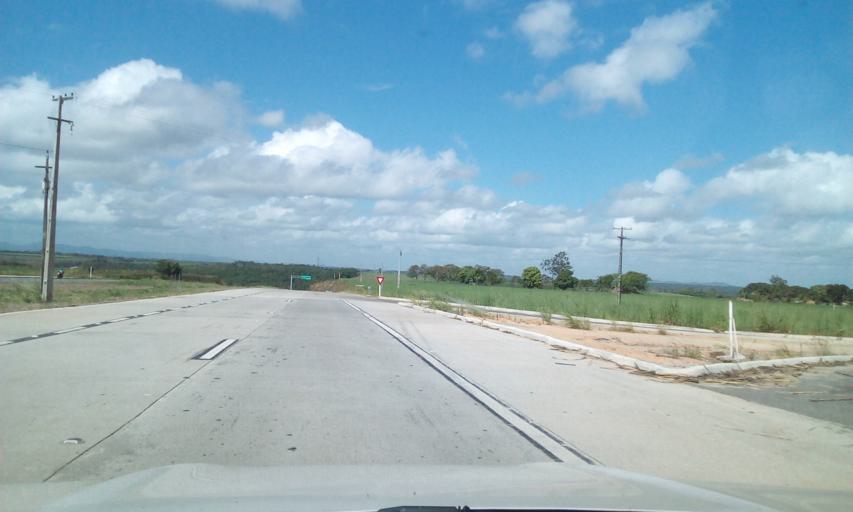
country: BR
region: Alagoas
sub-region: Rio Largo
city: Rio Largo
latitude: -9.4798
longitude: -35.8849
